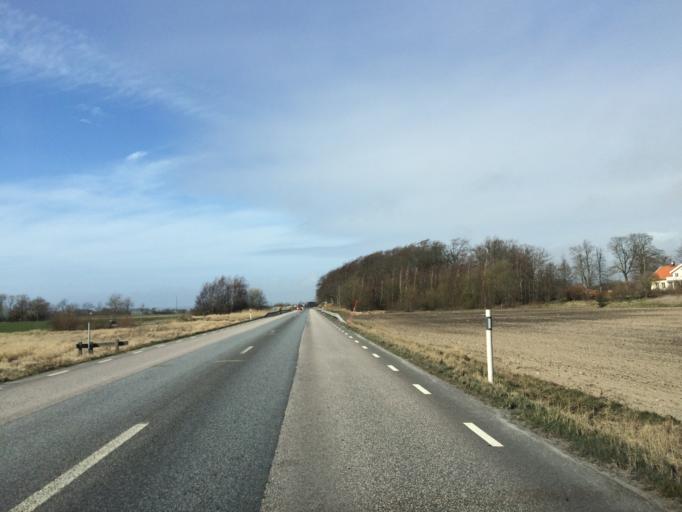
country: SE
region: Halland
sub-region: Halmstads Kommun
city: Paarp
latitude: 56.6003
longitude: 12.9686
